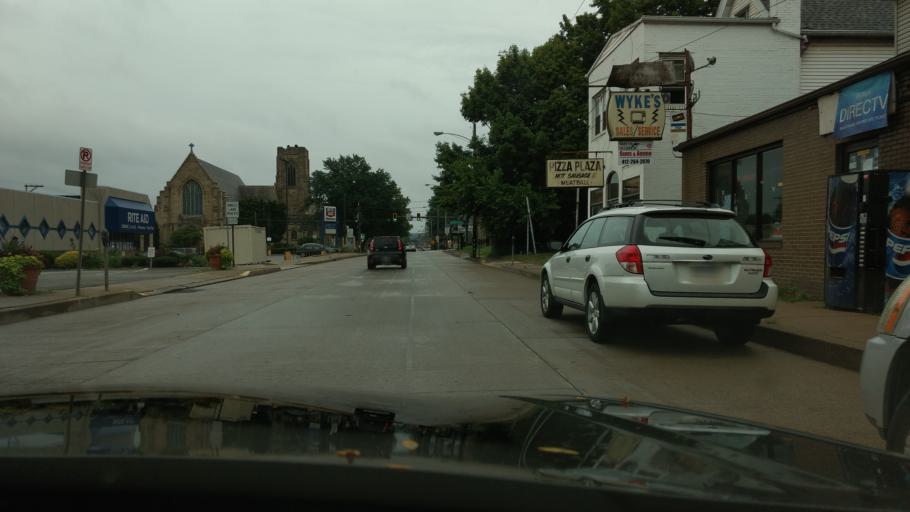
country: US
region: Pennsylvania
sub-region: Allegheny County
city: Coraopolis
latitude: 40.5167
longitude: -80.1624
